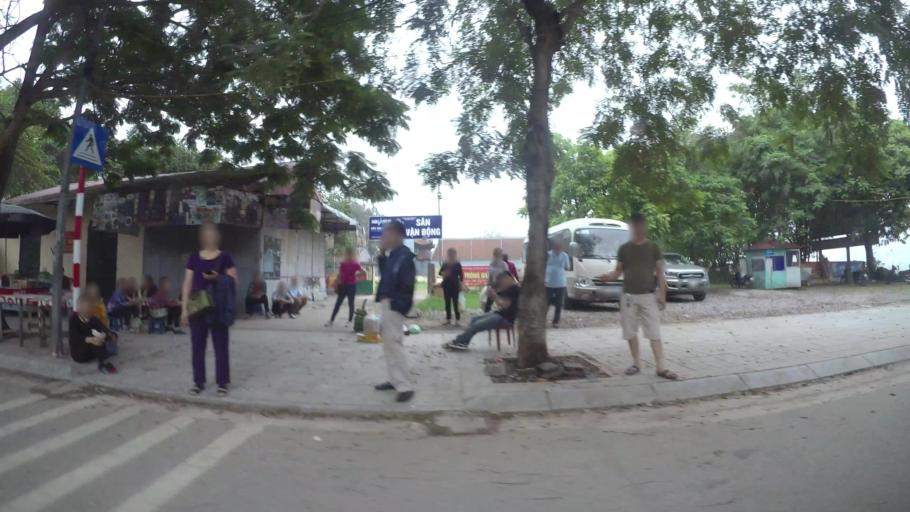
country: VN
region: Ha Noi
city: Tay Ho
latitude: 21.0571
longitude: 105.8202
